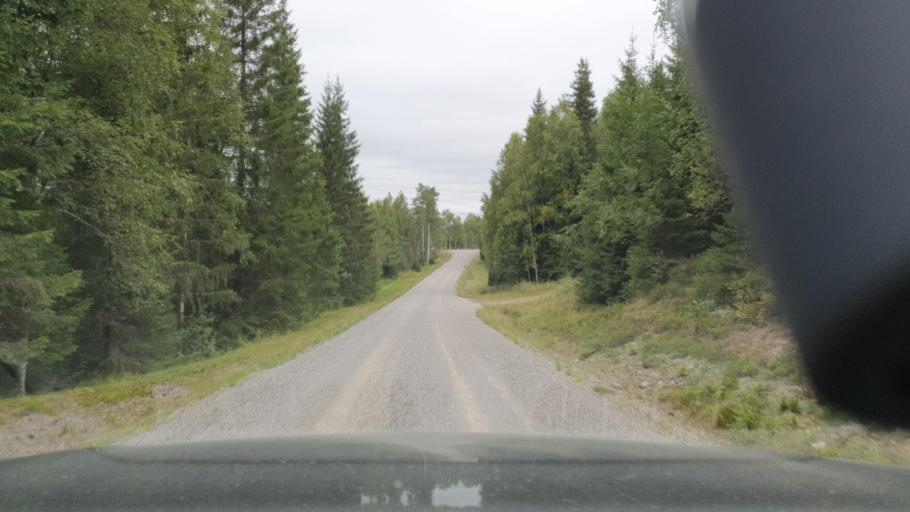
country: SE
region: Vaermland
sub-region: Eda Kommun
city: Charlottenberg
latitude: 60.1027
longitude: 12.6076
